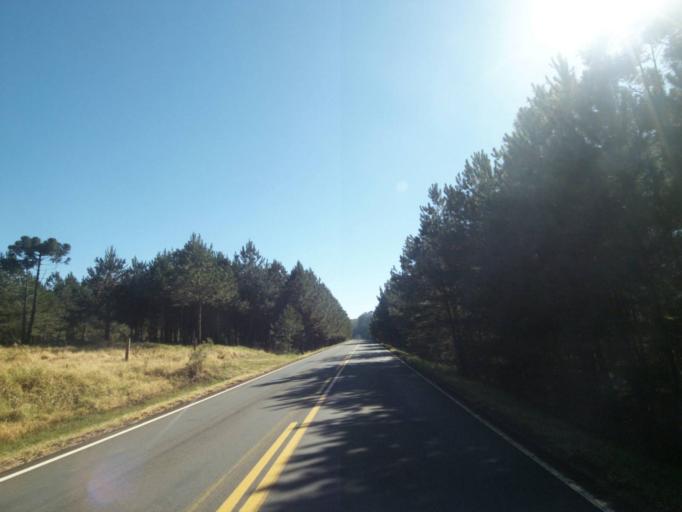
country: BR
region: Parana
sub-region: Telemaco Borba
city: Telemaco Borba
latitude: -24.4437
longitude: -50.5491
